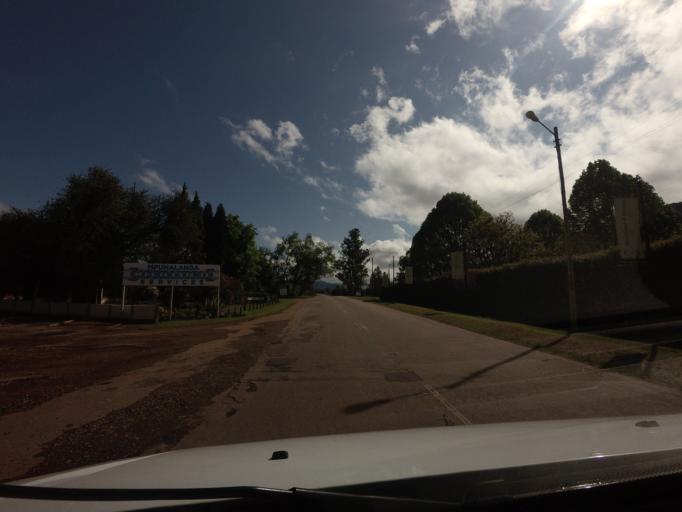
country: ZA
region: Mpumalanga
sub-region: Ehlanzeni District
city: Graksop
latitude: -25.0928
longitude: 30.7731
